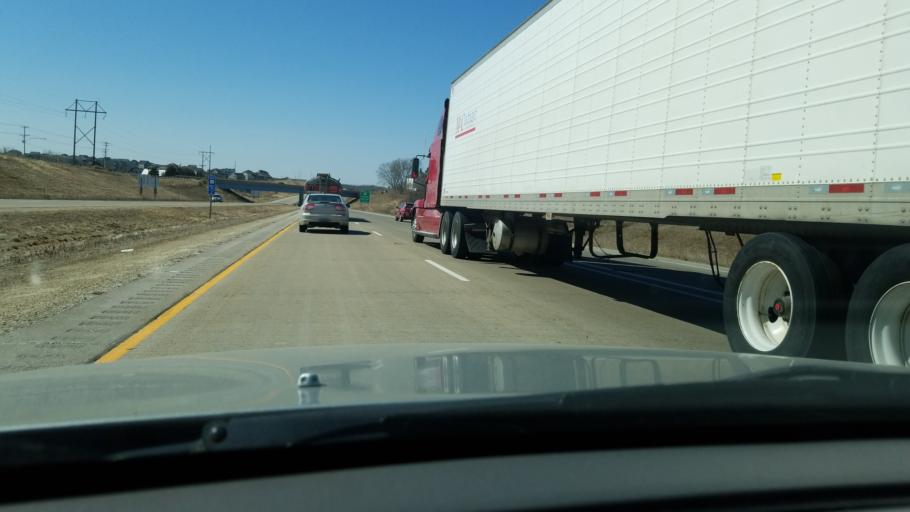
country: US
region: Wisconsin
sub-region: Dane County
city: Verona
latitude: 42.9733
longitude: -89.5199
